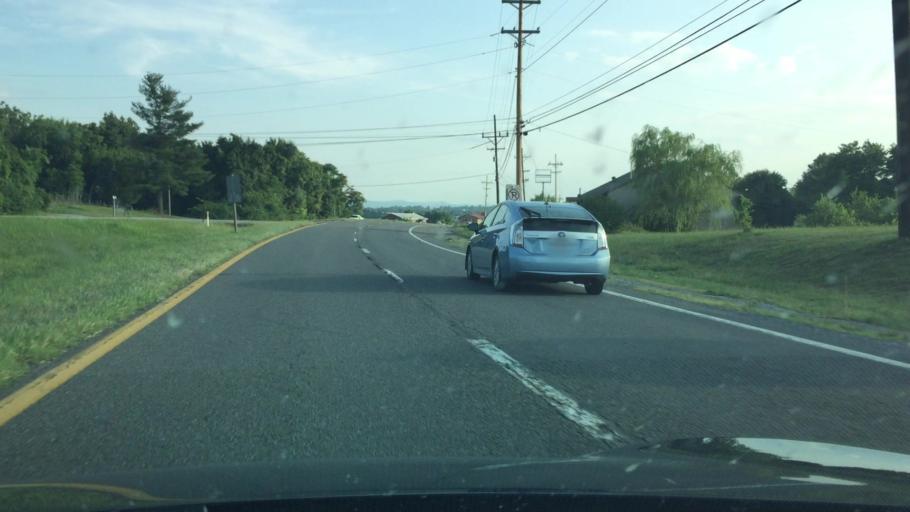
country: US
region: Virginia
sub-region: Pulaski County
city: Fairlawn
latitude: 37.1438
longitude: -80.6035
